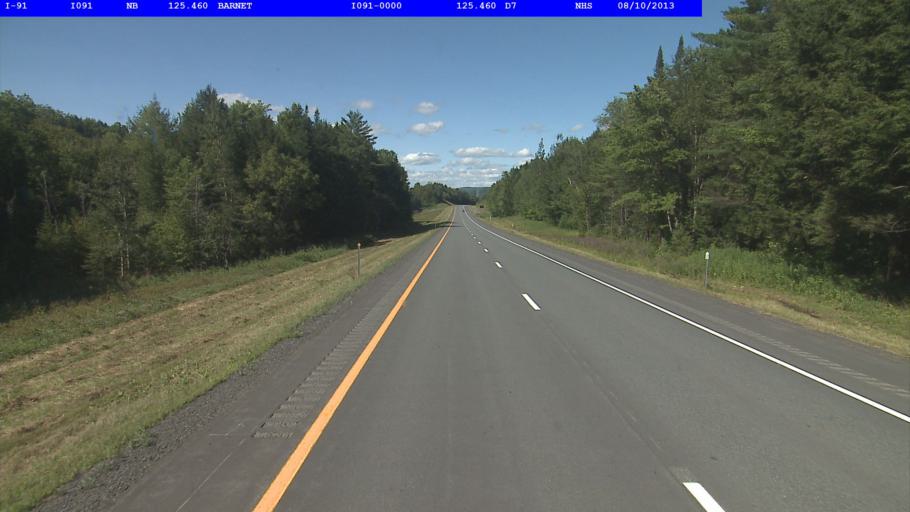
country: US
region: Vermont
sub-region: Caledonia County
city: Saint Johnsbury
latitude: 44.3587
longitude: -72.0324
